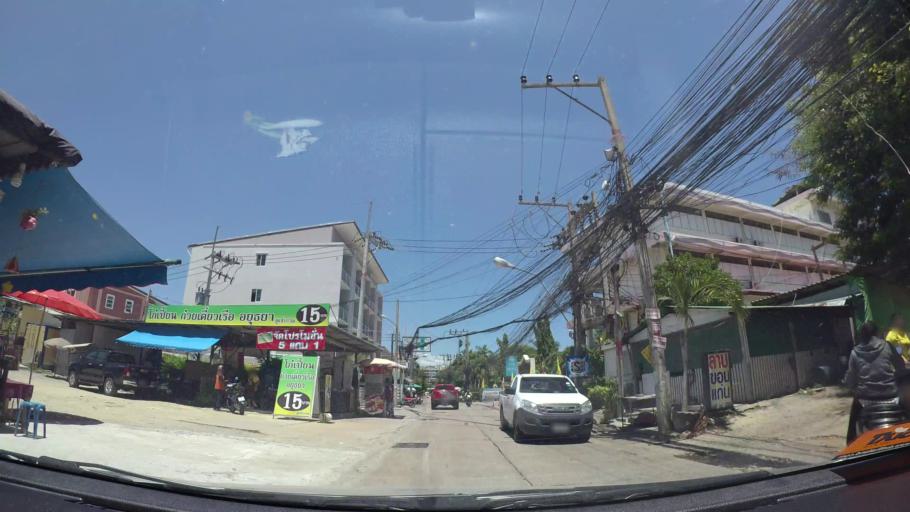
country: TH
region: Chon Buri
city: Phatthaya
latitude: 12.9322
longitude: 100.8942
